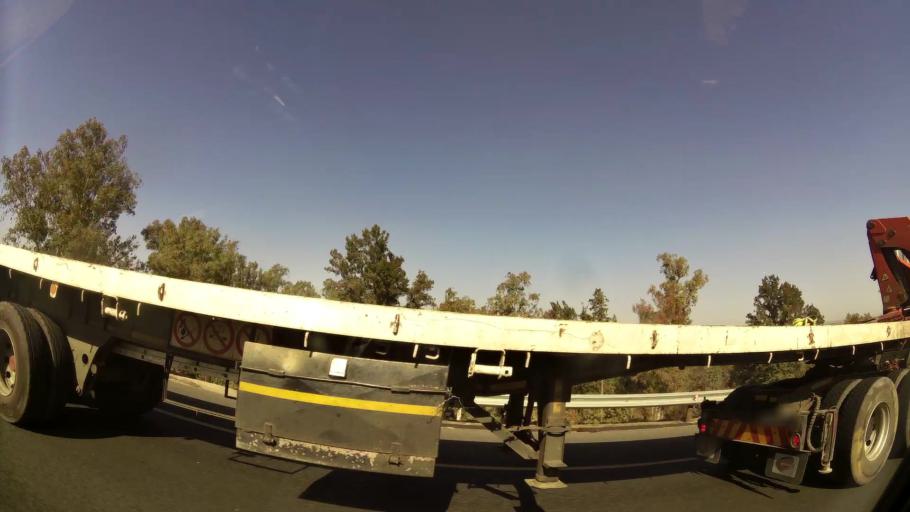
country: ZA
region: Gauteng
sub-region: City of Johannesburg Metropolitan Municipality
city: Diepsloot
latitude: -25.9436
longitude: 27.9618
